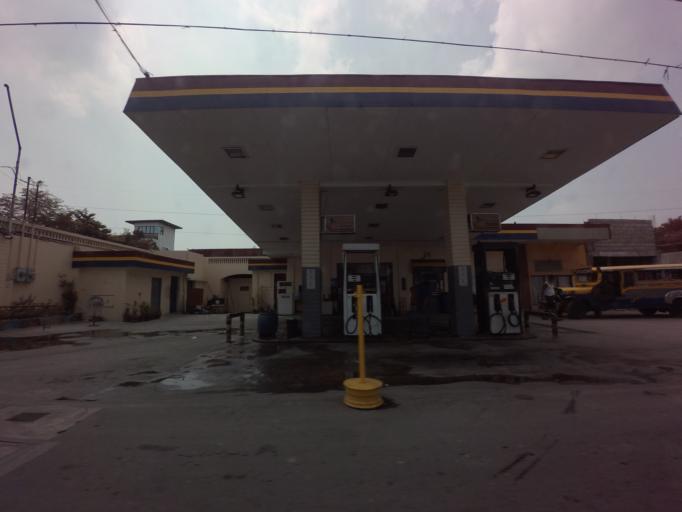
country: PH
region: Calabarzon
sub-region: Province of Rizal
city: Taguig
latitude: 14.4693
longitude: 121.0573
